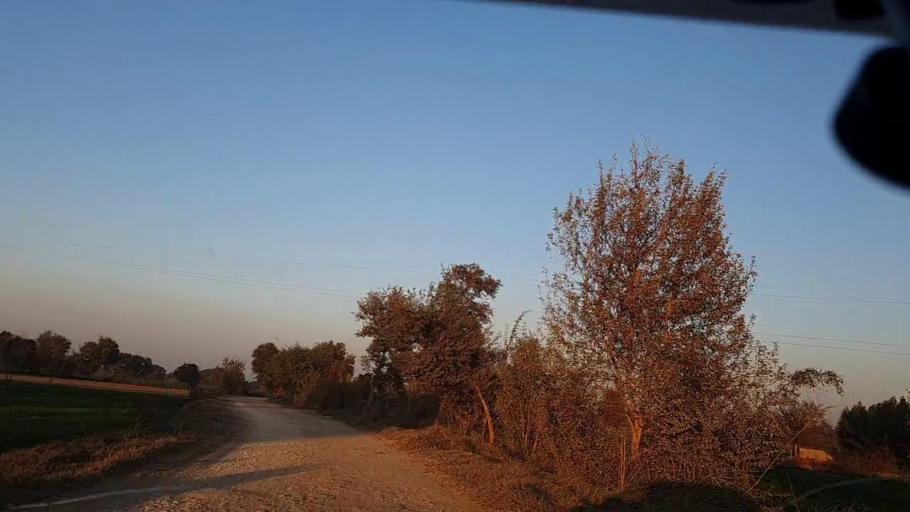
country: PK
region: Sindh
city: Adilpur
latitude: 27.8316
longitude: 69.2950
